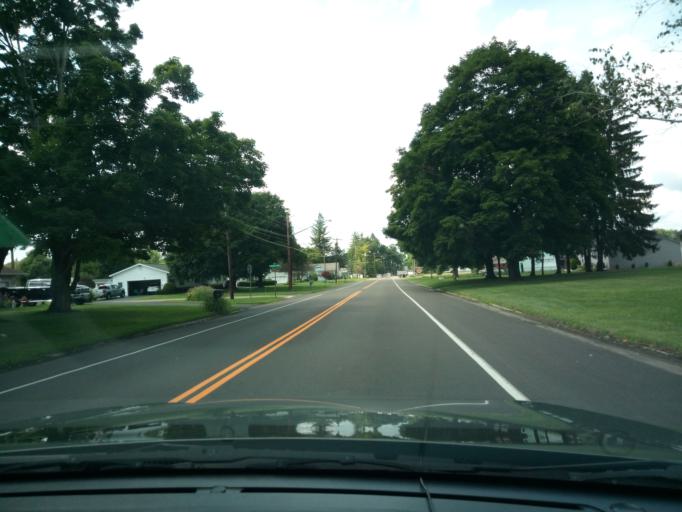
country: US
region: New York
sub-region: Chemung County
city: Southport
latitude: 42.0550
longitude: -76.7810
